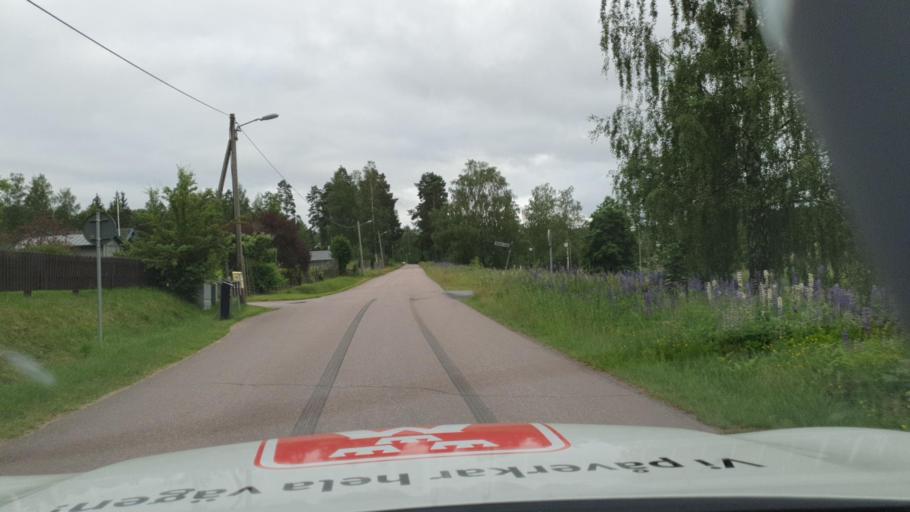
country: SE
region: Vaermland
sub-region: Kils Kommun
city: Kil
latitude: 59.5241
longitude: 13.3319
